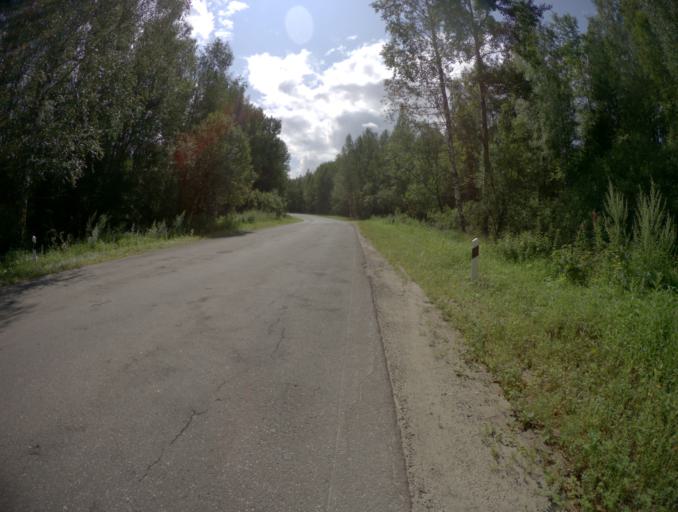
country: RU
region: Vladimir
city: Raduzhnyy
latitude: 55.9686
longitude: 40.2443
